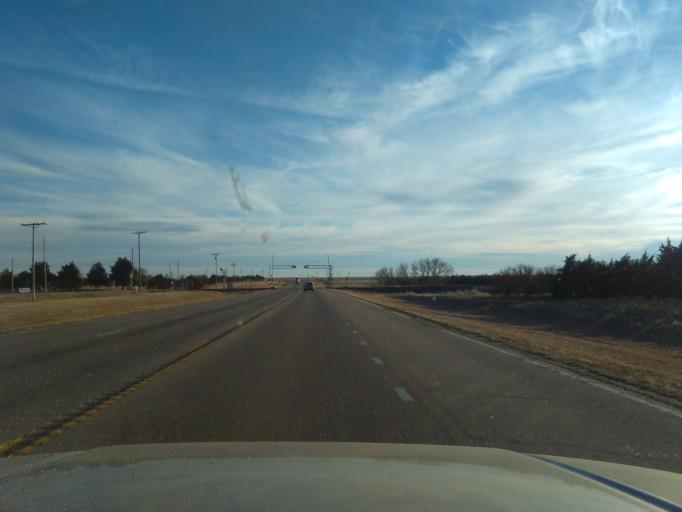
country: US
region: Kansas
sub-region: Logan County
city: Oakley
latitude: 39.1253
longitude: -100.8684
